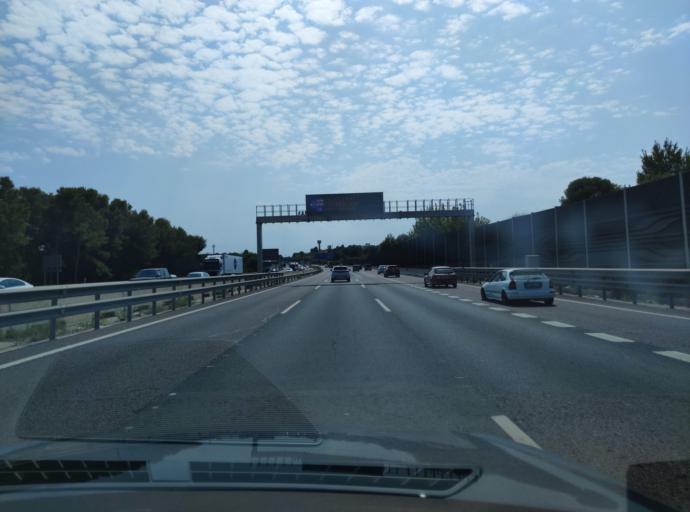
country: ES
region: Valencia
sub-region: Provincia de Valencia
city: Manises
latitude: 39.5252
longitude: -0.4703
